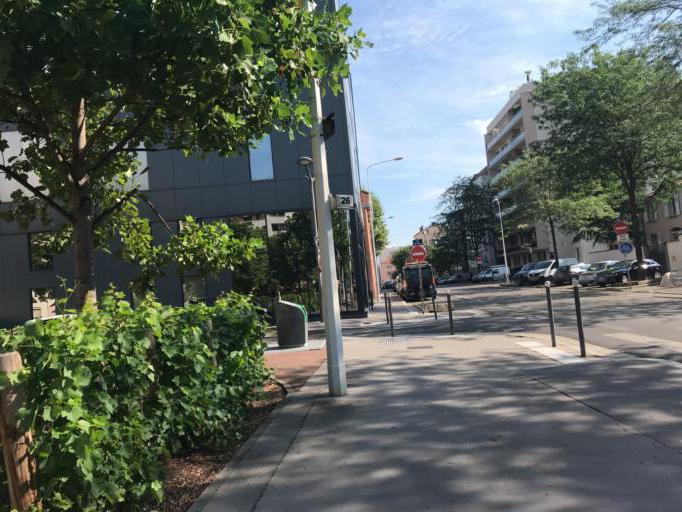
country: FR
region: Rhone-Alpes
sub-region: Departement du Rhone
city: Villeurbanne
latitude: 45.7483
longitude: 4.8727
